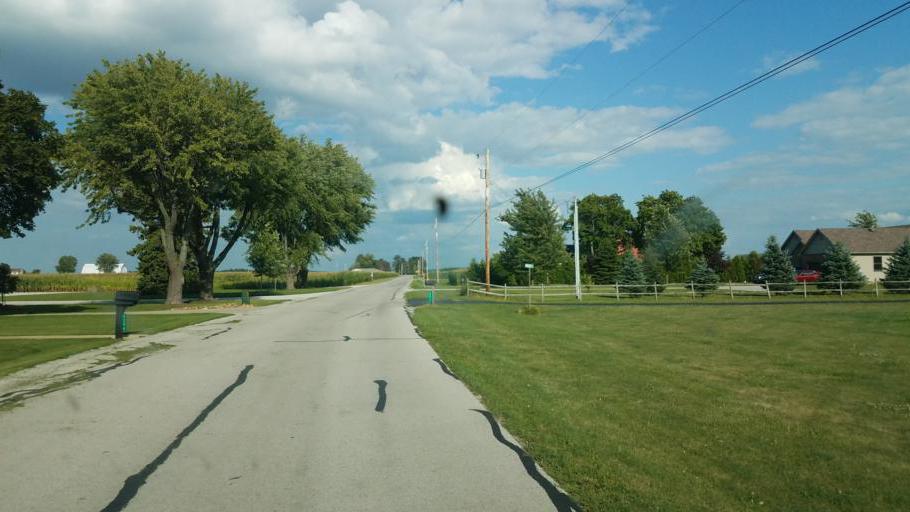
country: US
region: Ohio
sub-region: Wood County
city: Bowling Green
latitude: 41.3631
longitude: -83.5777
